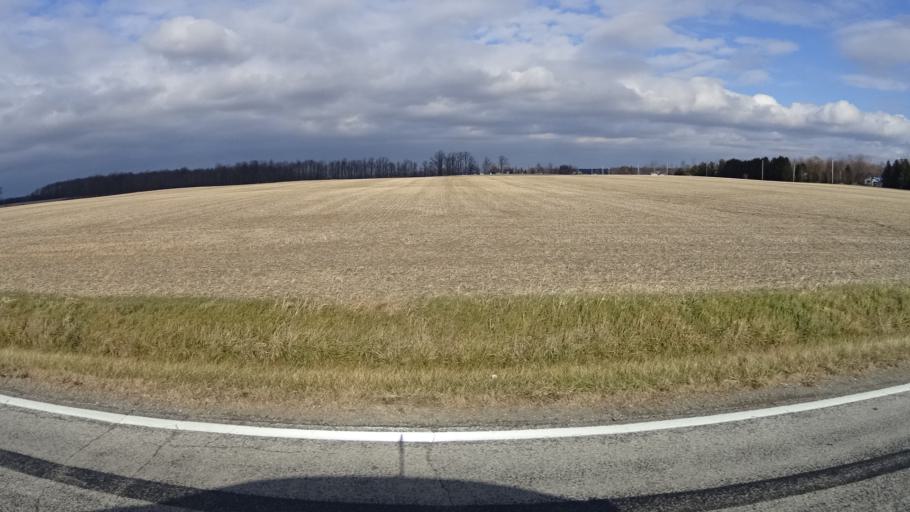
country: US
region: Ohio
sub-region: Lorain County
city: Camden
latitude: 41.2048
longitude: -82.2776
